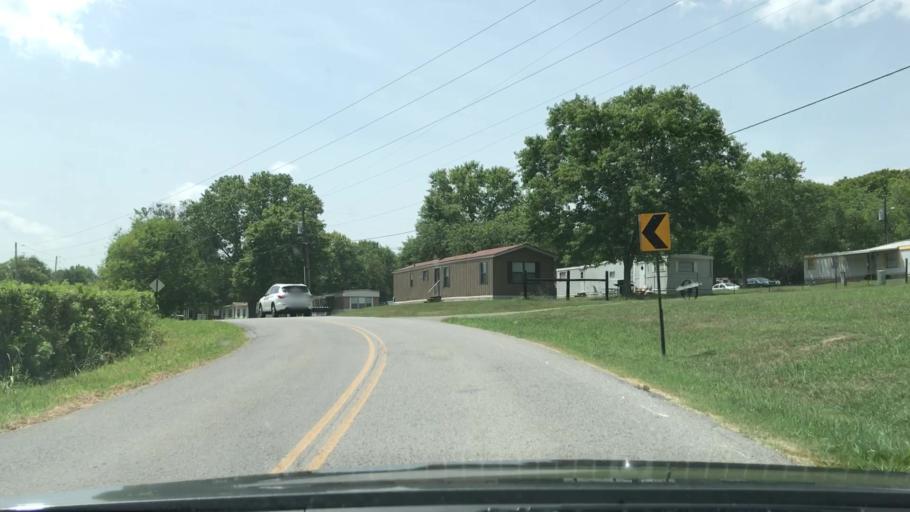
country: US
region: Tennessee
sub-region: Rutherford County
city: La Vergne
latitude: 35.9753
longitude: -86.5854
